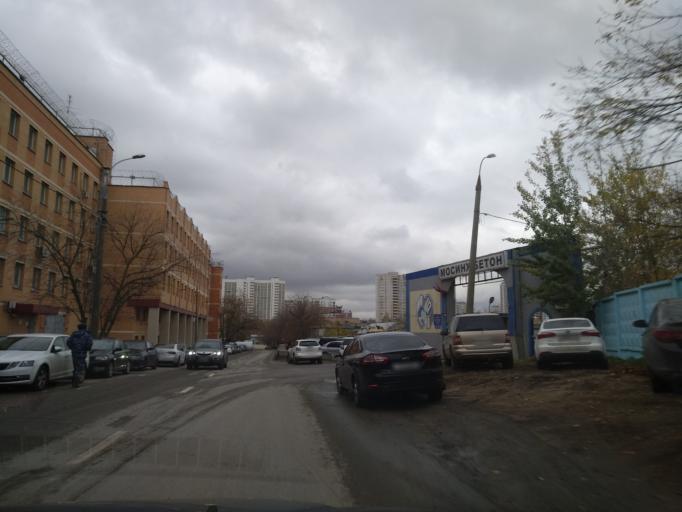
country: RU
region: Moscow
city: Kozeyevo
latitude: 55.8830
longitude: 37.6300
